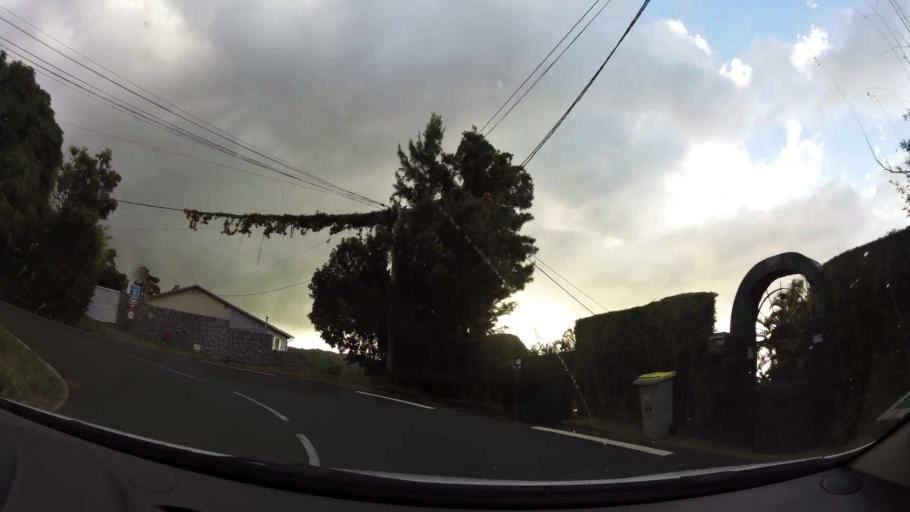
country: RE
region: Reunion
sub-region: Reunion
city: Saint-Denis
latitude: -20.9110
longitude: 55.4402
